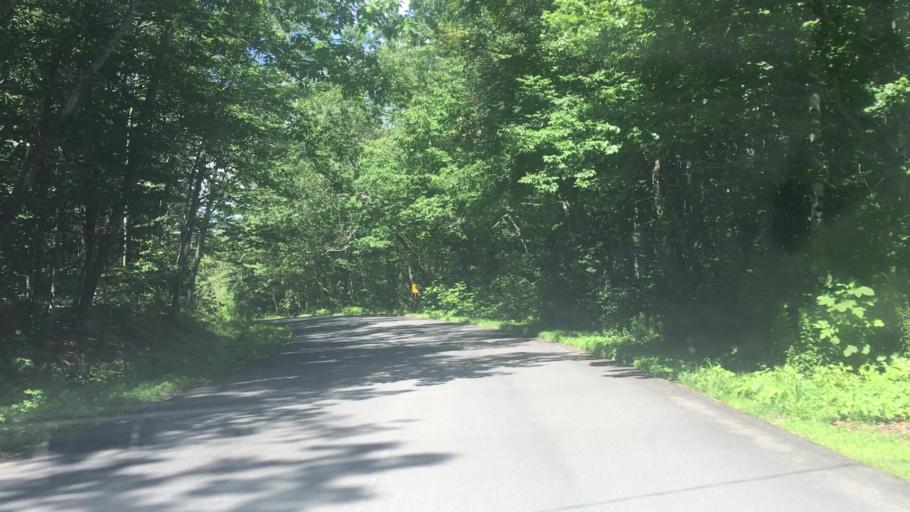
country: US
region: Maine
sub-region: Waldo County
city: Northport
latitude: 44.3810
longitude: -68.9718
